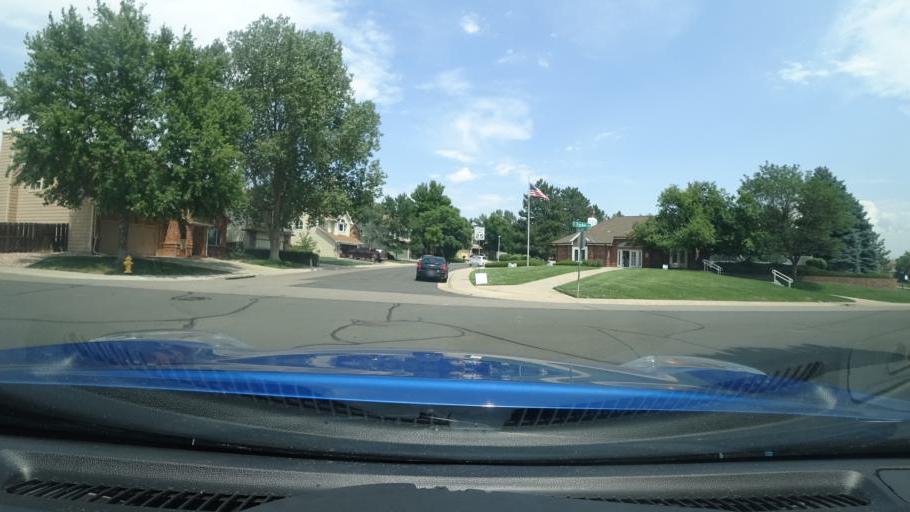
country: US
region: Colorado
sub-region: Adams County
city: Aurora
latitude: 39.6711
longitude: -104.7763
